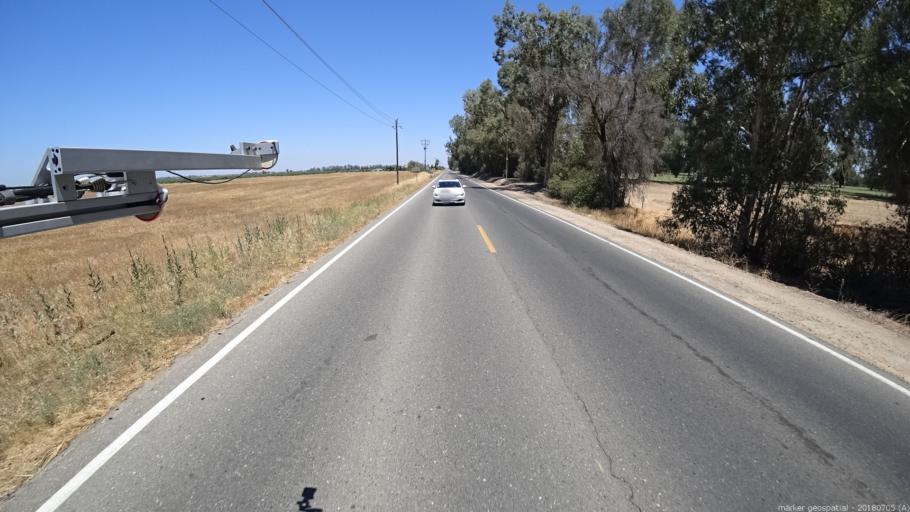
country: US
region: California
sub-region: Madera County
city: Madera Acres
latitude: 37.0260
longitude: -120.0744
